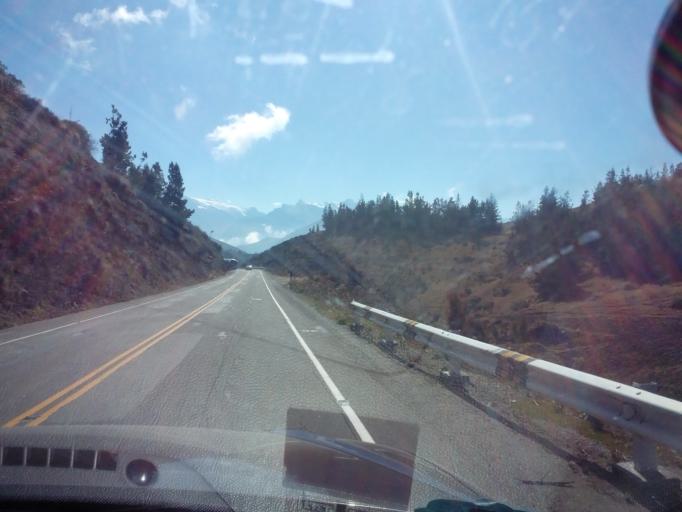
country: PE
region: Apurimac
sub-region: Provincia de Abancay
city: Cachora
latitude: -13.5636
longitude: -72.8210
